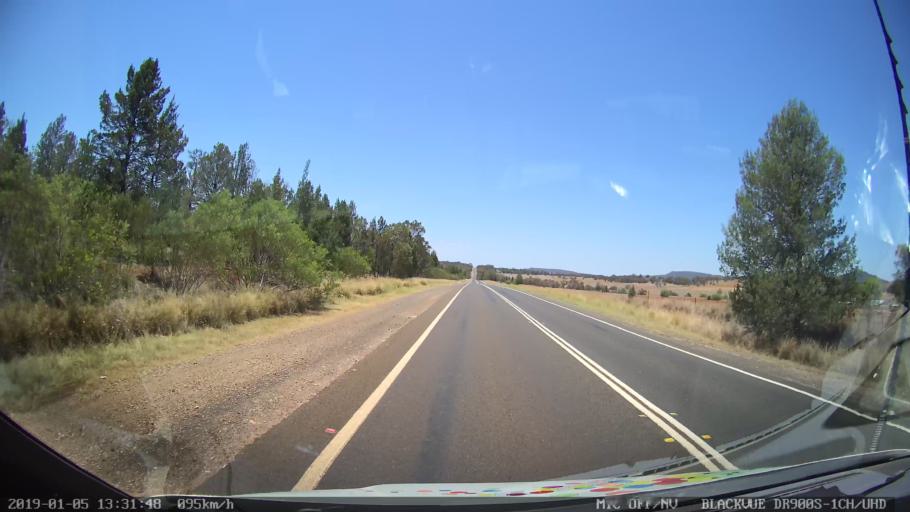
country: AU
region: New South Wales
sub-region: Gunnedah
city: Gunnedah
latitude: -31.0088
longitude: 150.0898
